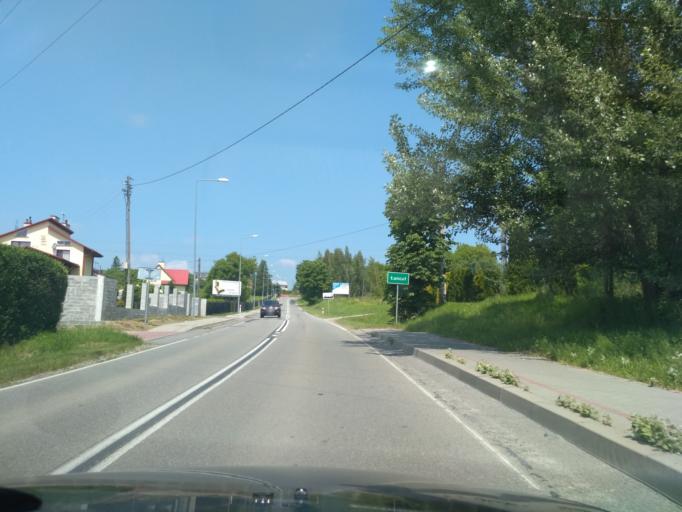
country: PL
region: Subcarpathian Voivodeship
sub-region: Powiat lancucki
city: Lancut
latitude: 50.0493
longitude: 22.2258
